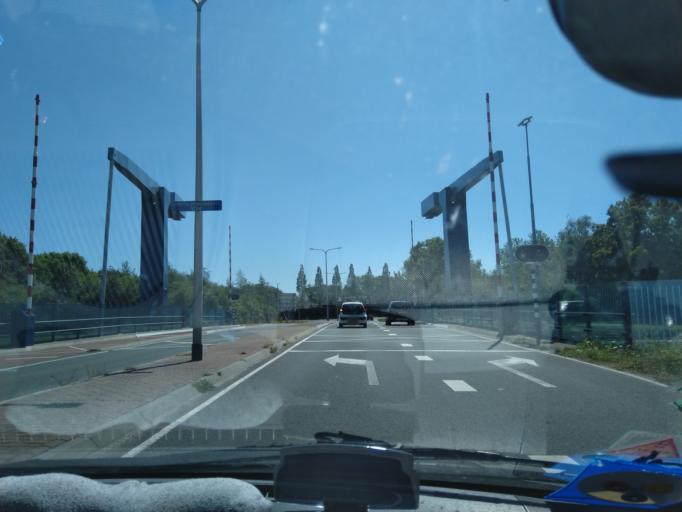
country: NL
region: Drenthe
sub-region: Gemeente Assen
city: Assen
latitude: 53.0000
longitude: 6.5323
